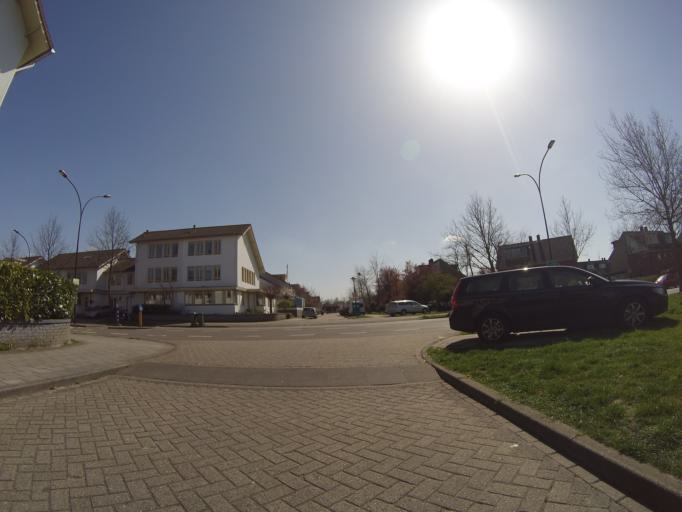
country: NL
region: Utrecht
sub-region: Gemeente Amersfoort
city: Hoogland
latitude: 52.1957
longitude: 5.3767
